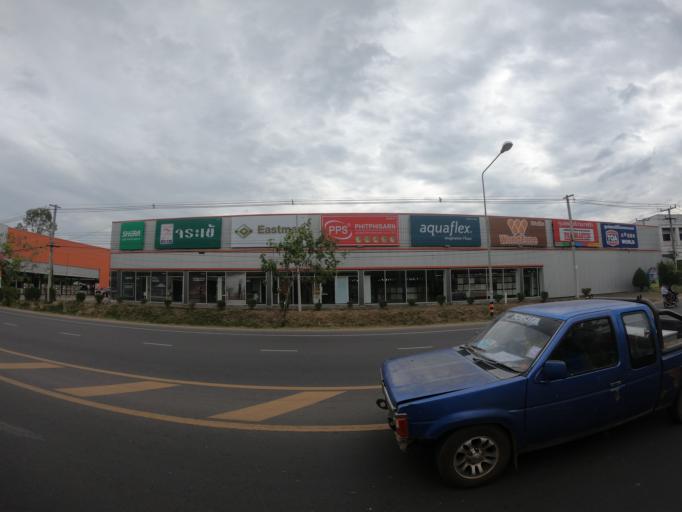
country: TH
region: Roi Et
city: Roi Et
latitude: 16.0701
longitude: 103.6784
